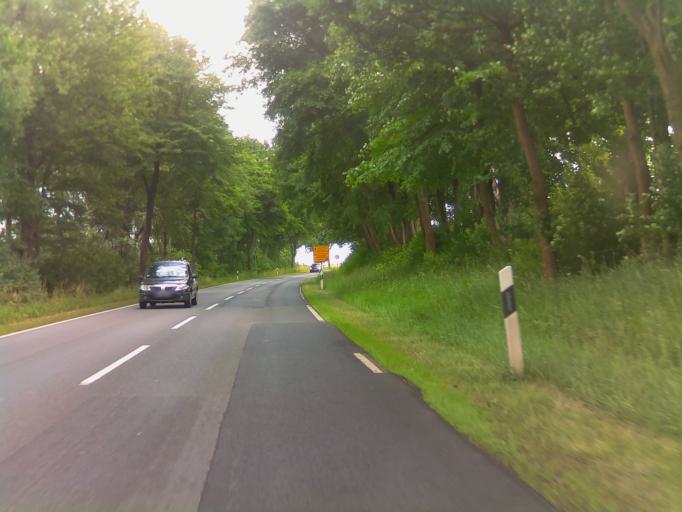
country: DE
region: Lower Saxony
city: Elze
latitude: 52.1697
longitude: 9.7048
